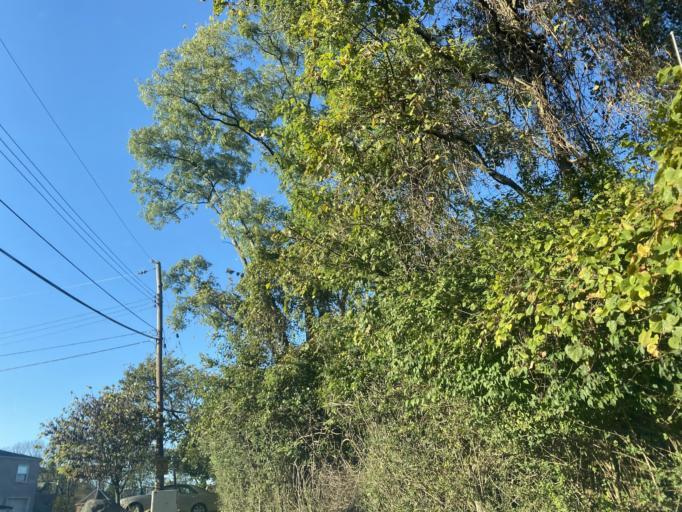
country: US
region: Kentucky
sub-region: Campbell County
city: Dayton
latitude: 39.1081
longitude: -84.4607
